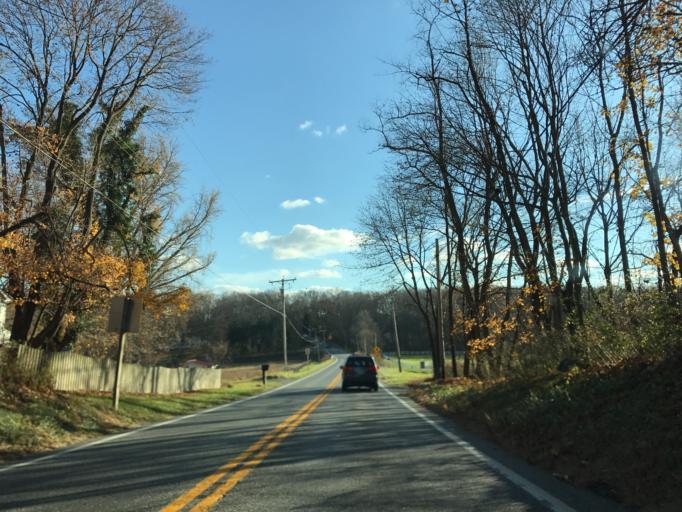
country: US
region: Maryland
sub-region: Harford County
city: Jarrettsville
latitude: 39.5983
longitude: -76.5128
